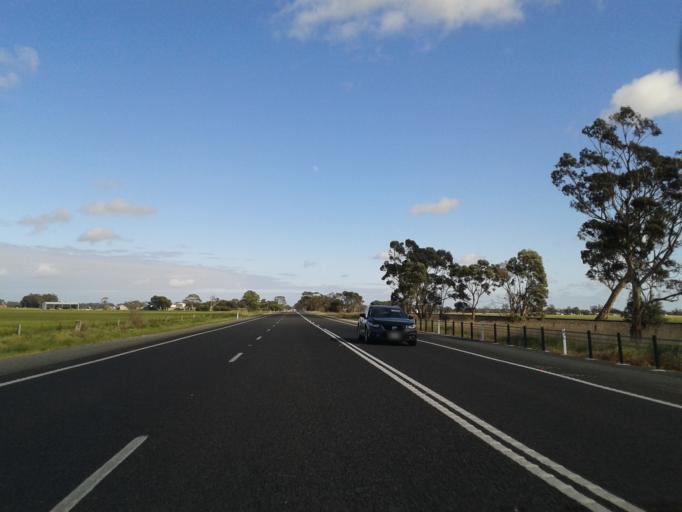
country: AU
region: South Australia
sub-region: Tatiara
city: Bordertown
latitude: -36.2741
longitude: 140.7141
